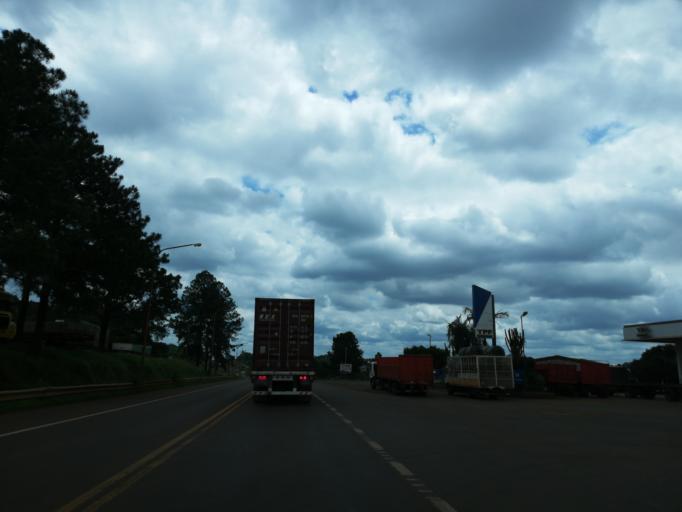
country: AR
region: Misiones
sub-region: Departamento de Leandro N. Alem
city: Leandro N. Alem
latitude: -27.6155
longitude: -55.3137
